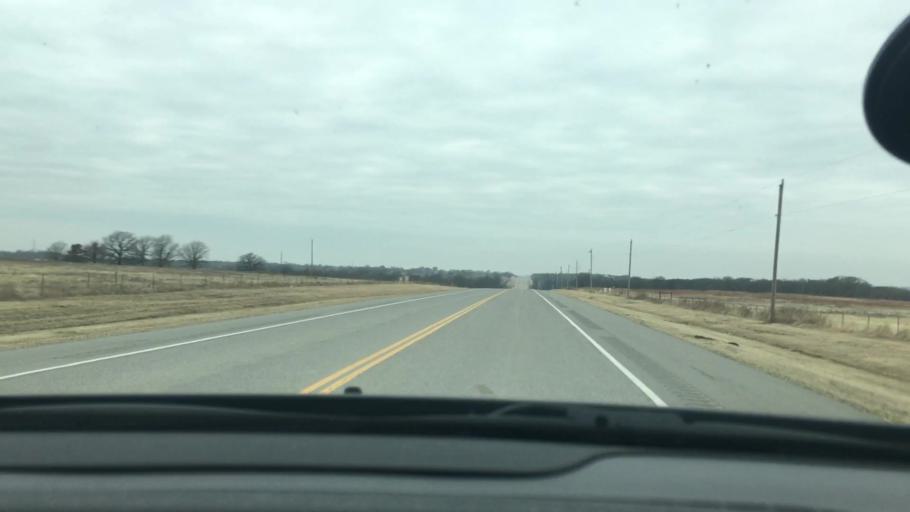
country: US
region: Oklahoma
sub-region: Garvin County
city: Wynnewood
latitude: 34.4925
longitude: -97.3938
